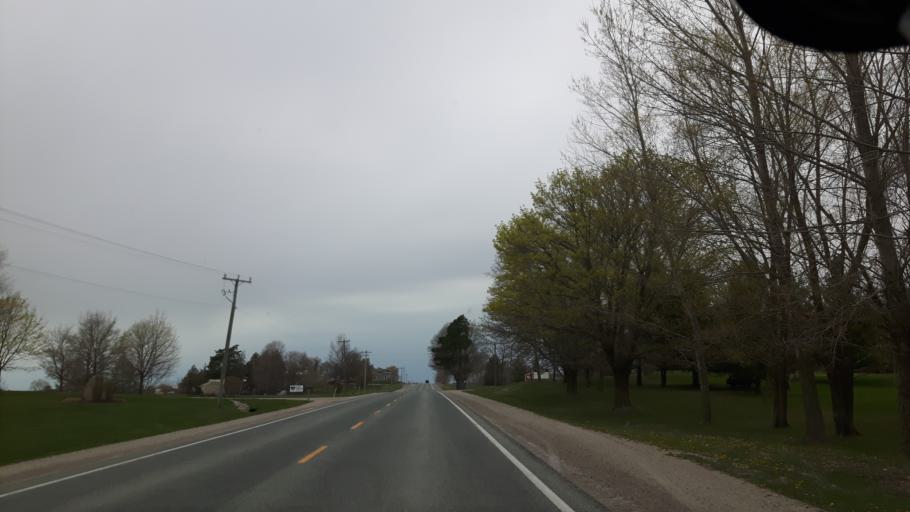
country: CA
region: Ontario
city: Bluewater
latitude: 43.6317
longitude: -81.5734
